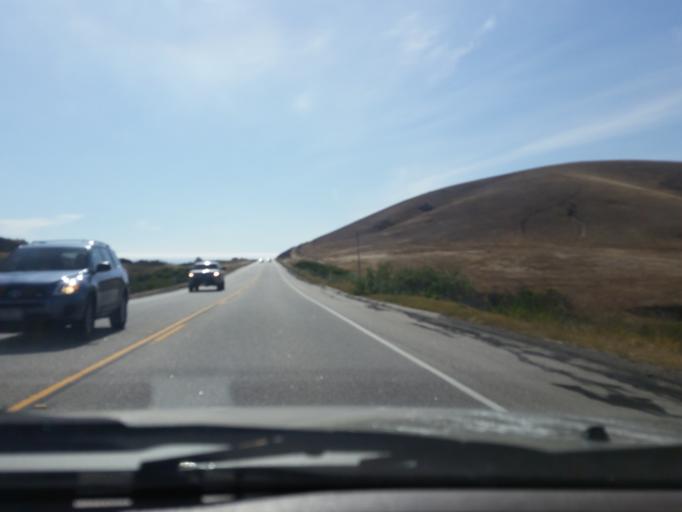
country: US
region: California
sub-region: San Luis Obispo County
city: Cayucos
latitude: 35.4501
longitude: -120.9330
